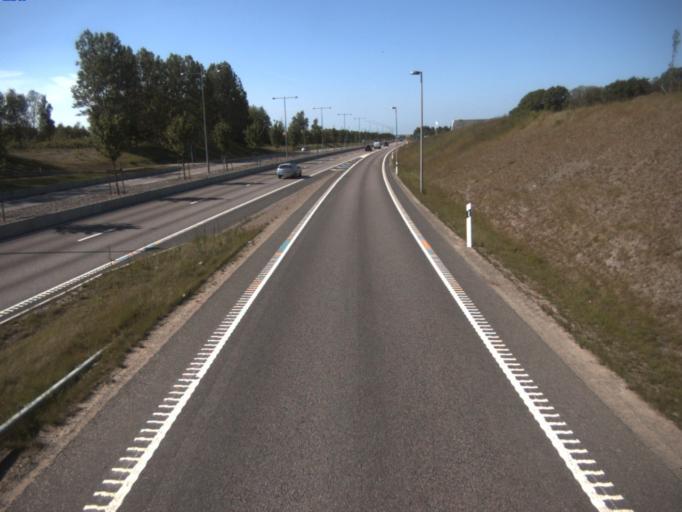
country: SE
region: Skane
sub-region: Helsingborg
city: Odakra
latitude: 56.0554
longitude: 12.7504
